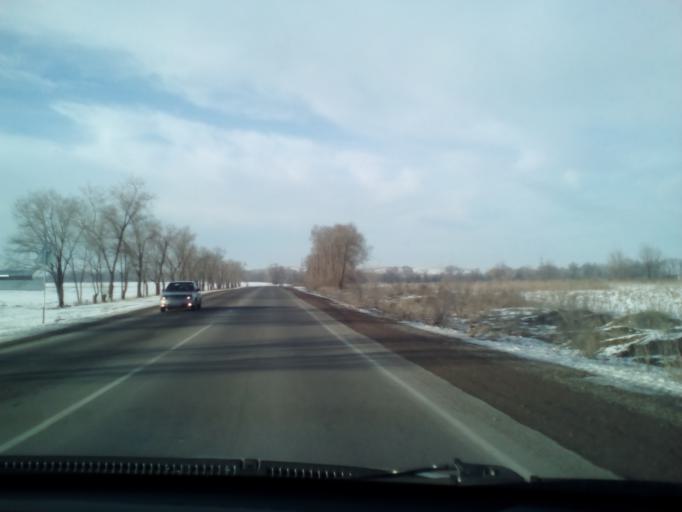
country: KZ
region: Almaty Oblysy
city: Burunday
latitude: 43.2160
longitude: 76.4136
